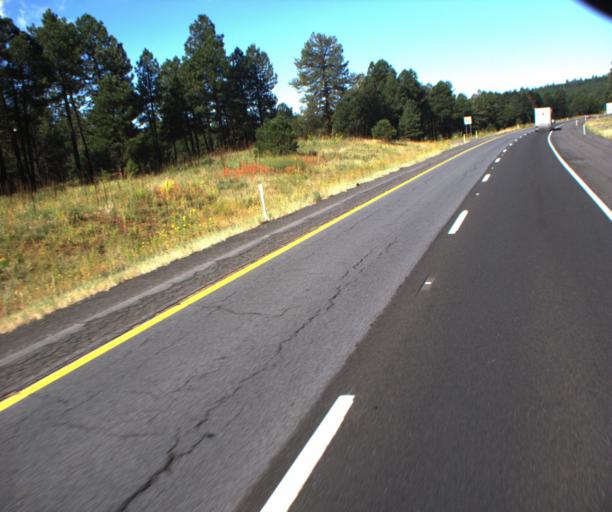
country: US
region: Arizona
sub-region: Coconino County
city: Parks
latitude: 35.2476
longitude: -111.8795
